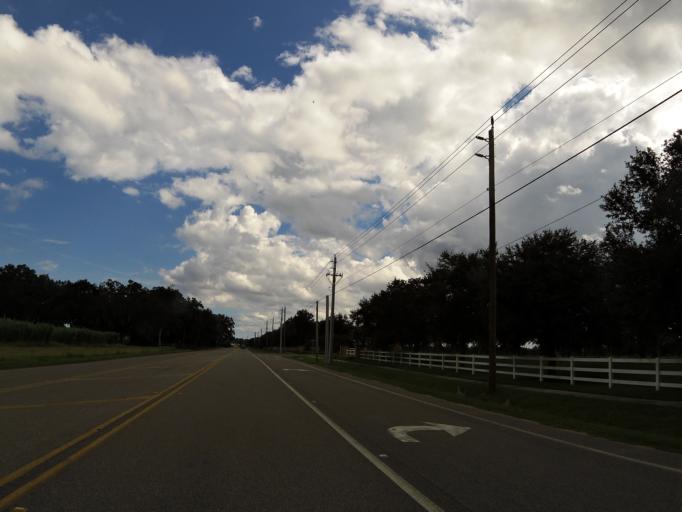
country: US
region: Florida
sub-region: Saint Johns County
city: Saint Augustine South
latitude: 29.8304
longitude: -81.4959
